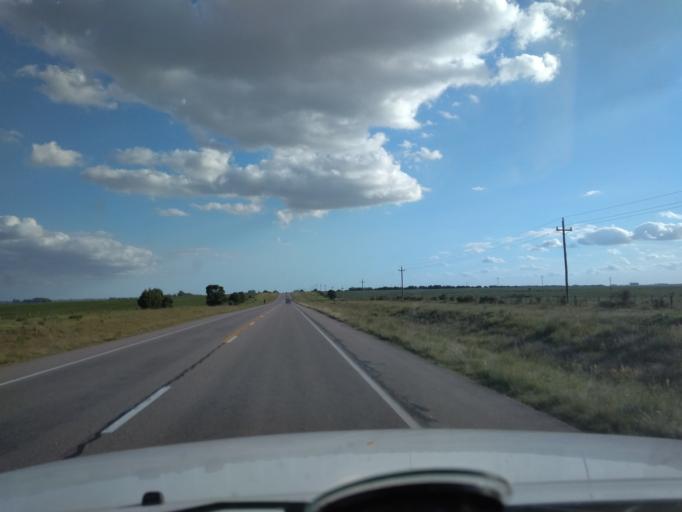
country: UY
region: Florida
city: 25 de Mayo
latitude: -34.2953
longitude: -56.2248
